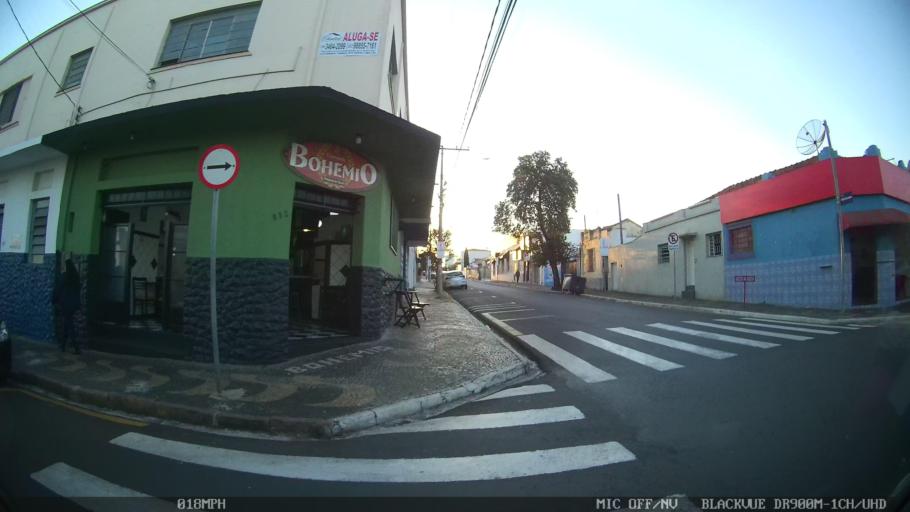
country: BR
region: Sao Paulo
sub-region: Santa Barbara D'Oeste
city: Santa Barbara d'Oeste
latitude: -22.7578
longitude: -47.4148
